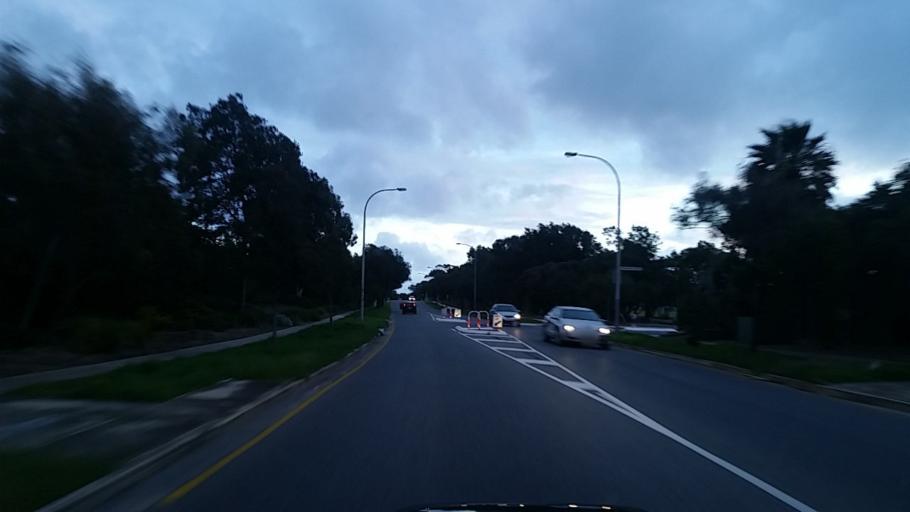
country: AU
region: South Australia
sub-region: Charles Sturt
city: West Lakes Shore
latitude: -34.8624
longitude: 138.4871
